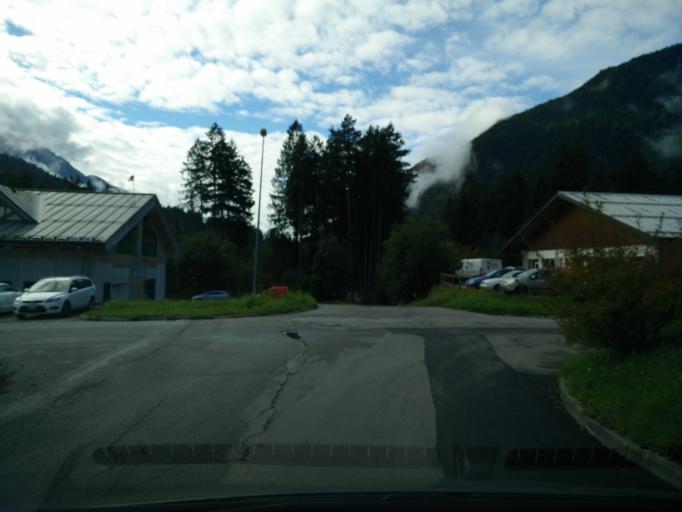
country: IT
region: Veneto
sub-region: Provincia di Belluno
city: Vigo di Cadore
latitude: 46.5112
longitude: 12.4635
